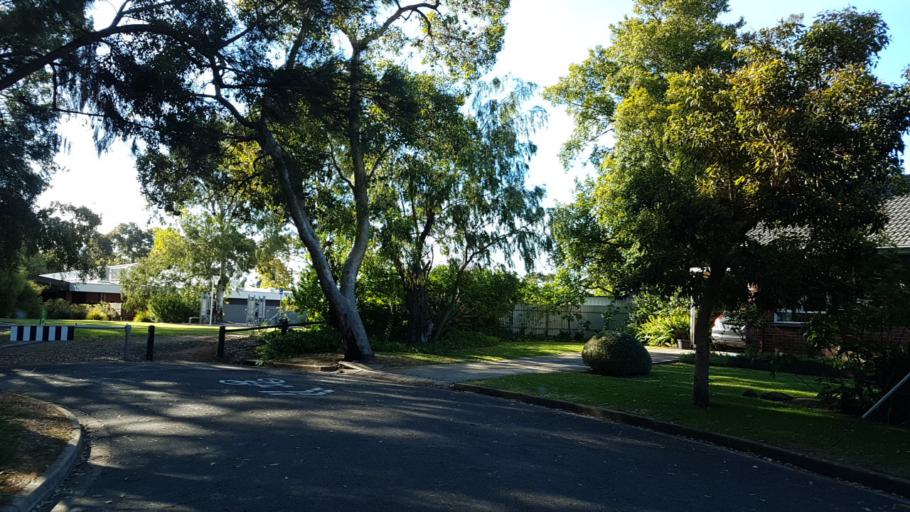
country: AU
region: South Australia
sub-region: Campbelltown
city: Campbelltown
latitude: -34.8898
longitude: 138.6779
